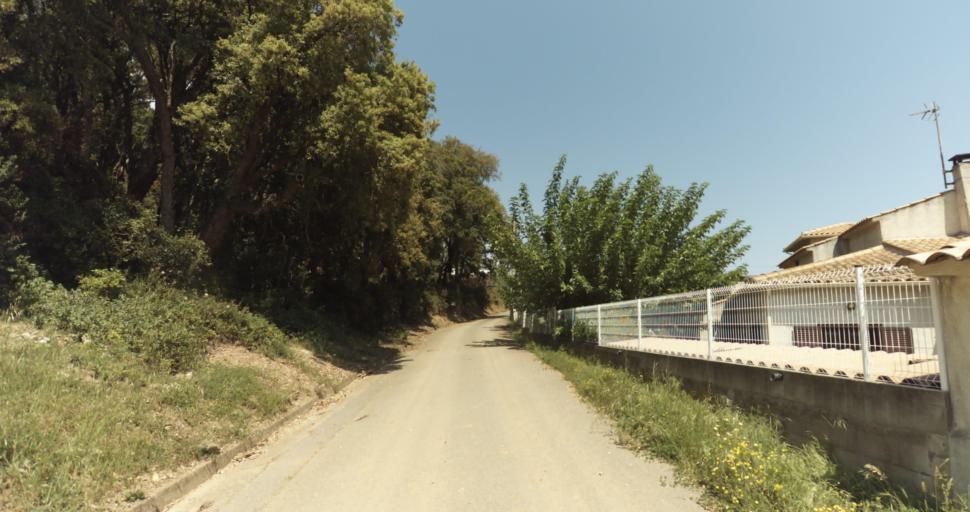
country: FR
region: Corsica
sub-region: Departement de la Haute-Corse
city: Biguglia
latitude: 42.5920
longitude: 9.4260
